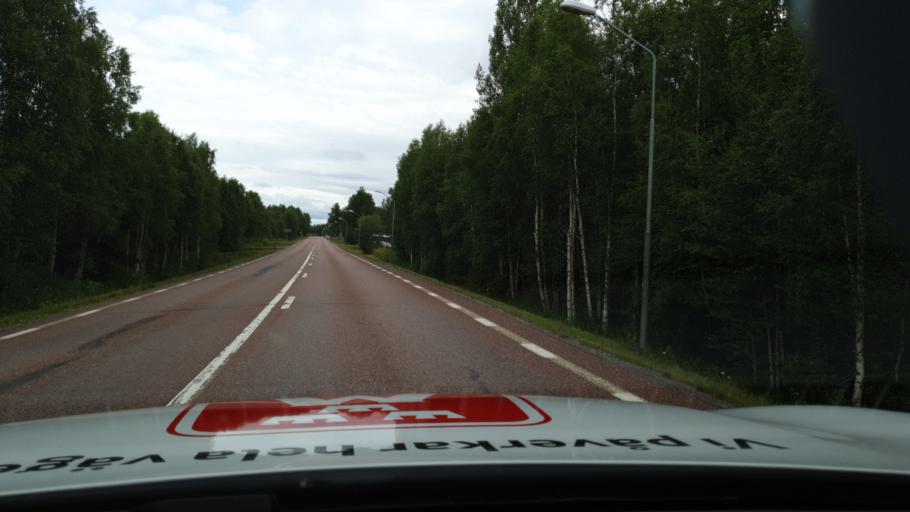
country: SE
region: Jaemtland
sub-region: Stroemsunds Kommun
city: Stroemsund
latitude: 63.9584
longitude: 15.8484
